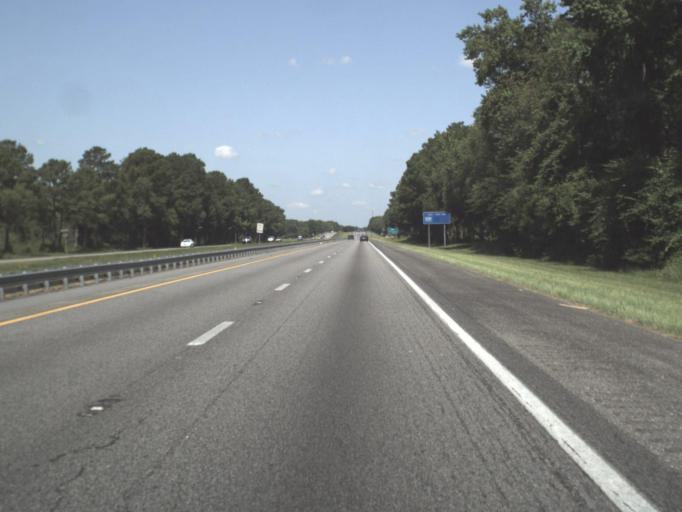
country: US
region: Florida
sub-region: Madison County
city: Madison
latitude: 30.4322
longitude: -83.6158
